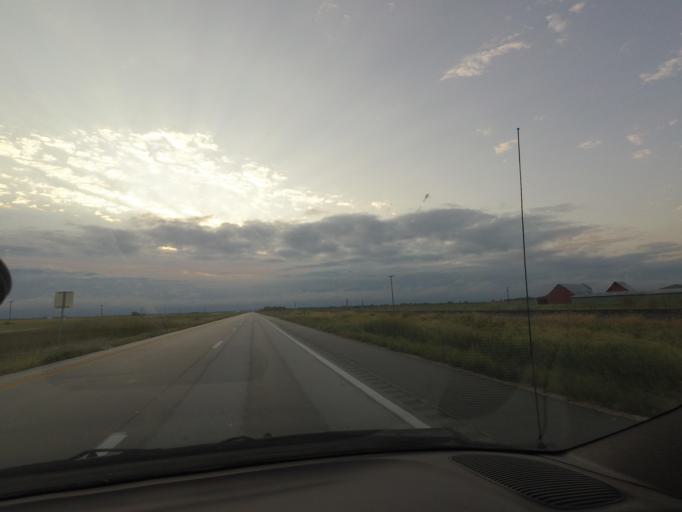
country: US
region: Missouri
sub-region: Shelby County
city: Shelbina
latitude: 39.7080
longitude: -92.1015
